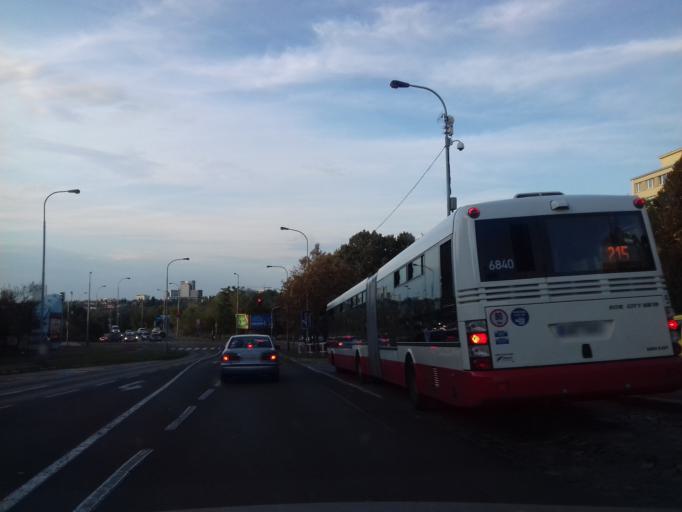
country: CZ
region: Praha
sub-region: Praha 4
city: Hodkovicky
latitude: 50.0272
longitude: 14.4514
